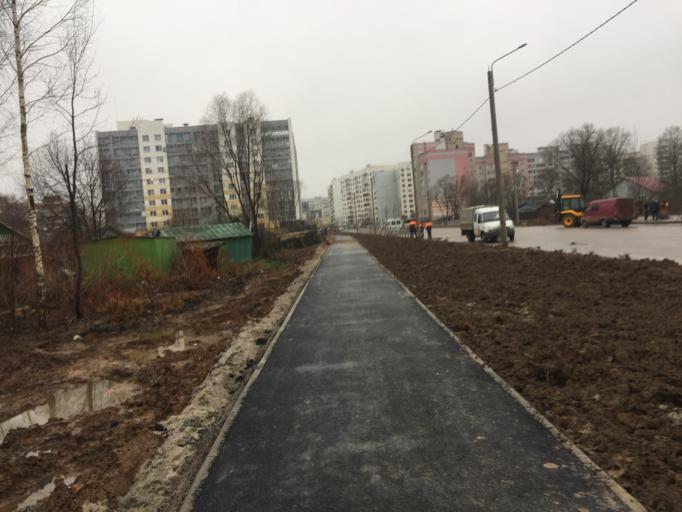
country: RU
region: Jaroslavl
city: Yaroslavl
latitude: 57.6978
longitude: 39.7862
